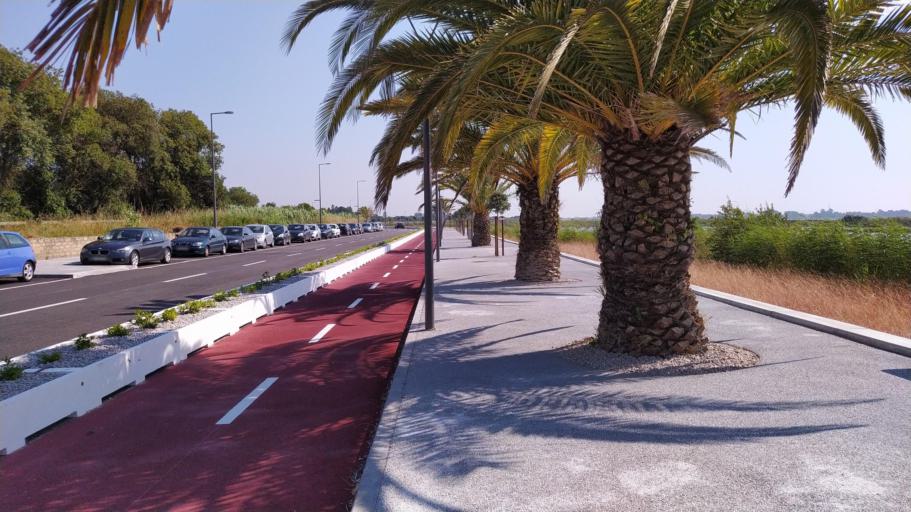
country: PT
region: Aveiro
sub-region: Aveiro
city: Aveiro
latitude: 40.6333
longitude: -8.6615
